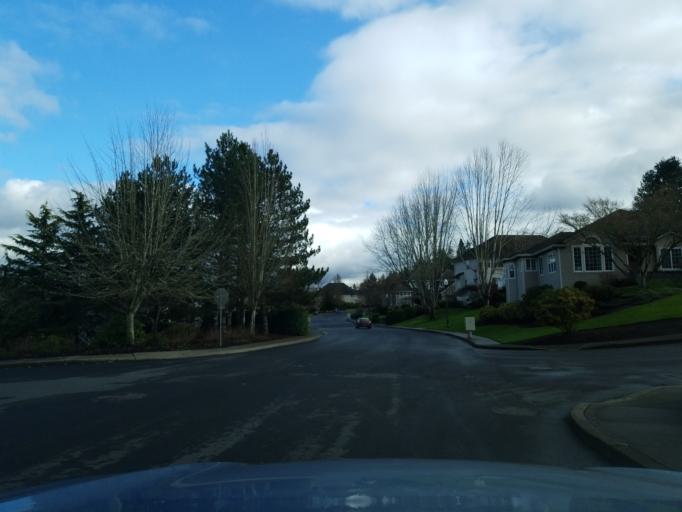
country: US
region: Washington
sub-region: Clark County
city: Felida
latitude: 45.7157
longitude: -122.7001
